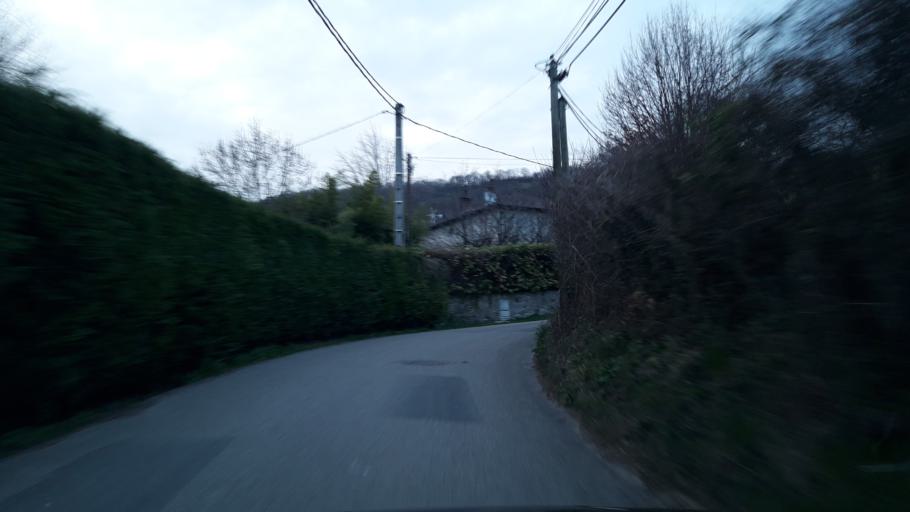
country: FR
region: Rhone-Alpes
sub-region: Departement de l'Isere
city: Herbeys
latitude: 45.1451
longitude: 5.7926
